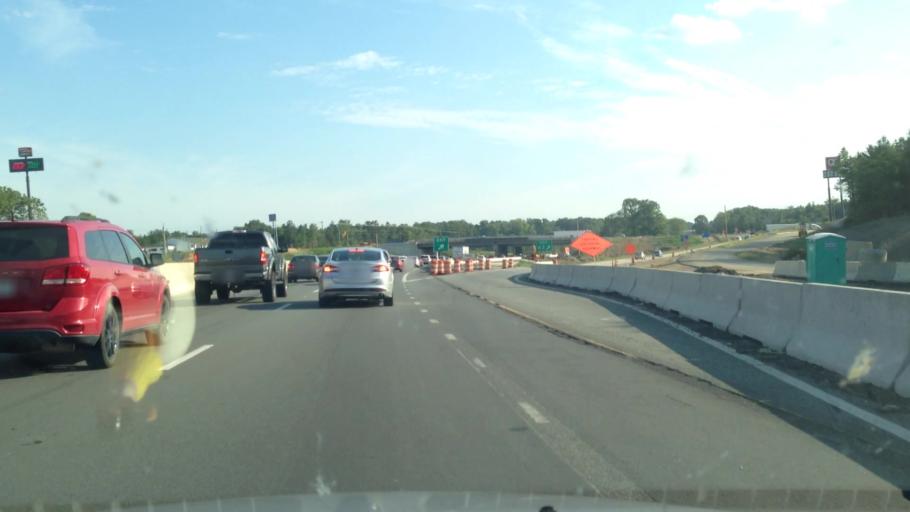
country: US
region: North Carolina
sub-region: Cabarrus County
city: Kannapolis
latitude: 35.5013
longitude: -80.5625
